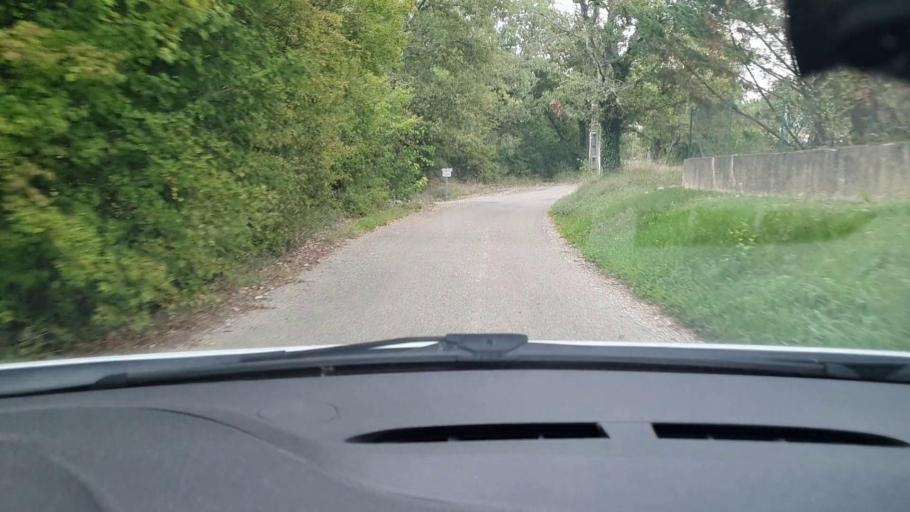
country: FR
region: Languedoc-Roussillon
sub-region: Departement du Gard
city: Mons
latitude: 44.1631
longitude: 4.2833
